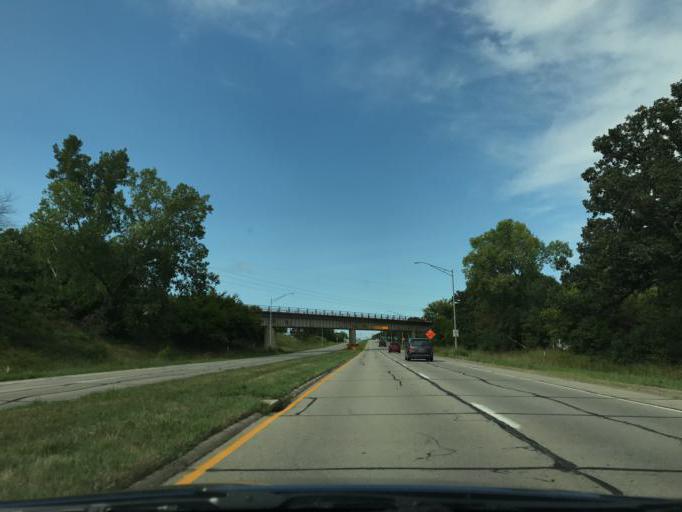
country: US
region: Iowa
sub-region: Jasper County
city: Newton
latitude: 41.6934
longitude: -93.0771
